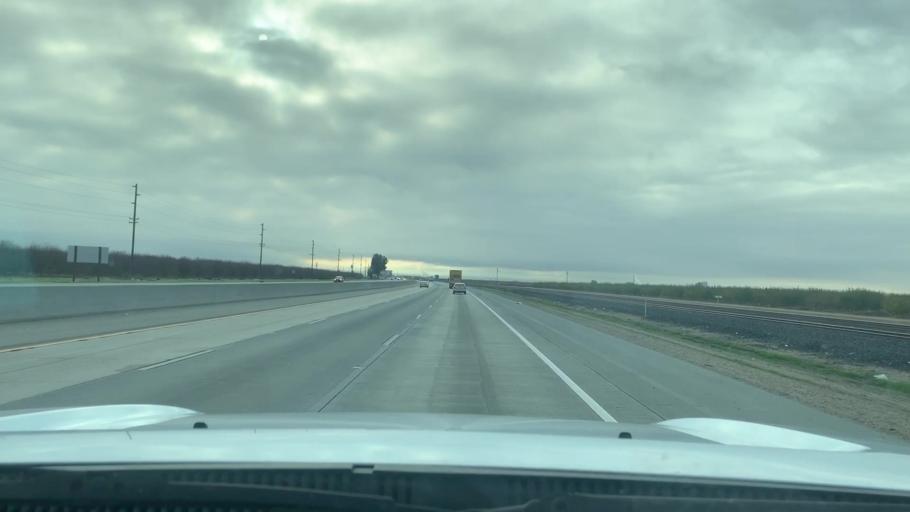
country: US
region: California
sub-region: Kern County
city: Shafter
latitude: 35.5183
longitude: -119.1840
